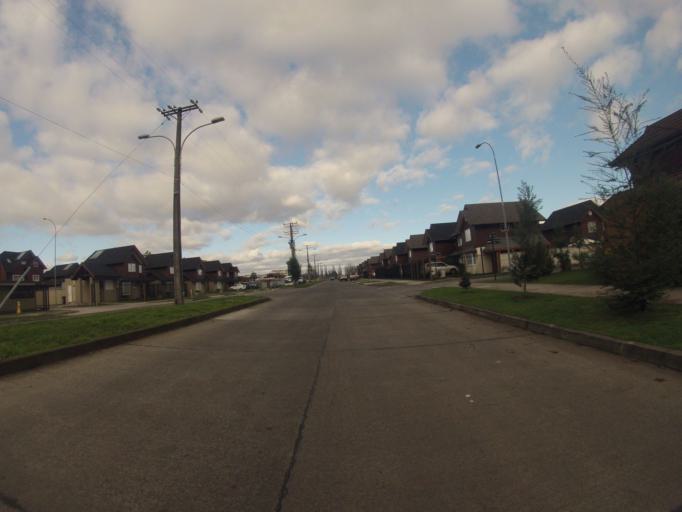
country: CL
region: Araucania
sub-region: Provincia de Cautin
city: Temuco
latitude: -38.7413
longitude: -72.6453
